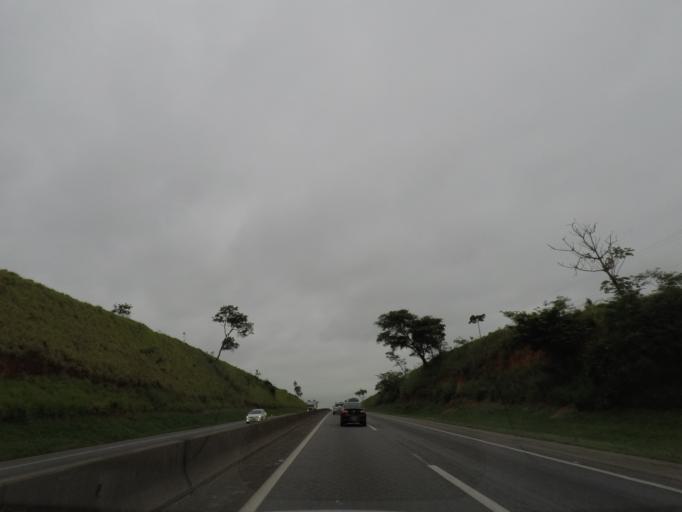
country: BR
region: Sao Paulo
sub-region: Pindamonhangaba
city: Pindamonhangaba
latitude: -22.9669
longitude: -45.4338
